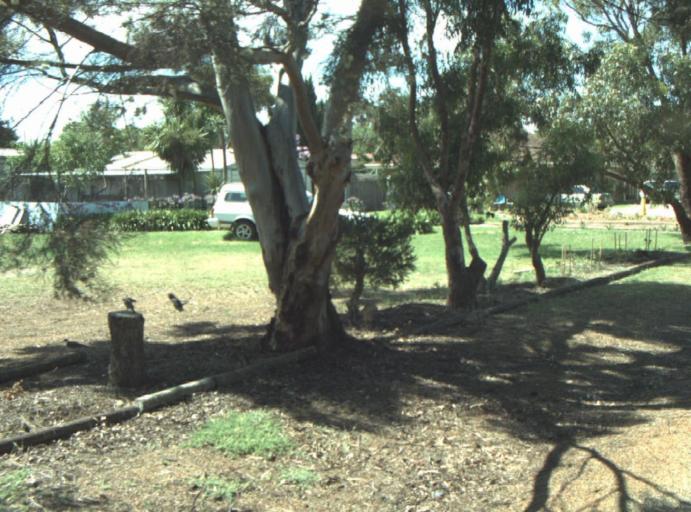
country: AU
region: Victoria
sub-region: Greater Geelong
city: East Geelong
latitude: -38.1710
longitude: 144.4170
